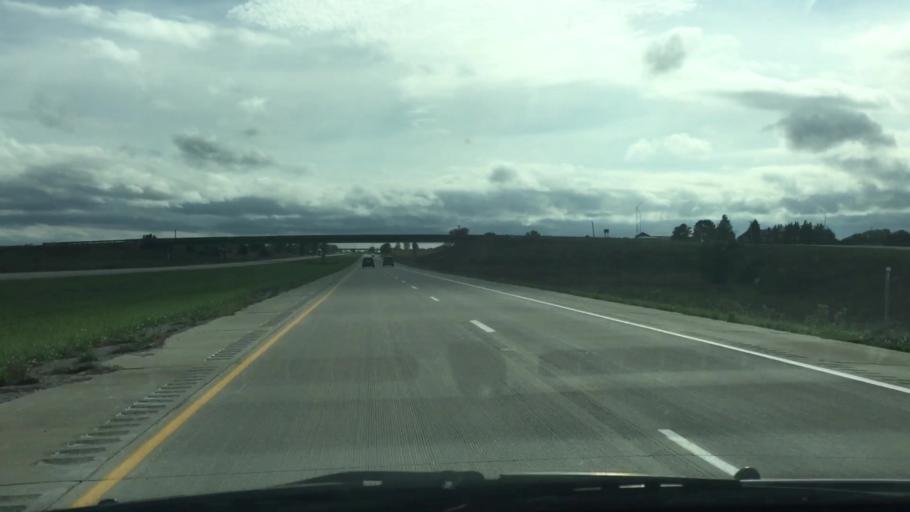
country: US
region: Iowa
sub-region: Decatur County
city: Leon
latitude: 40.8141
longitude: -93.8264
